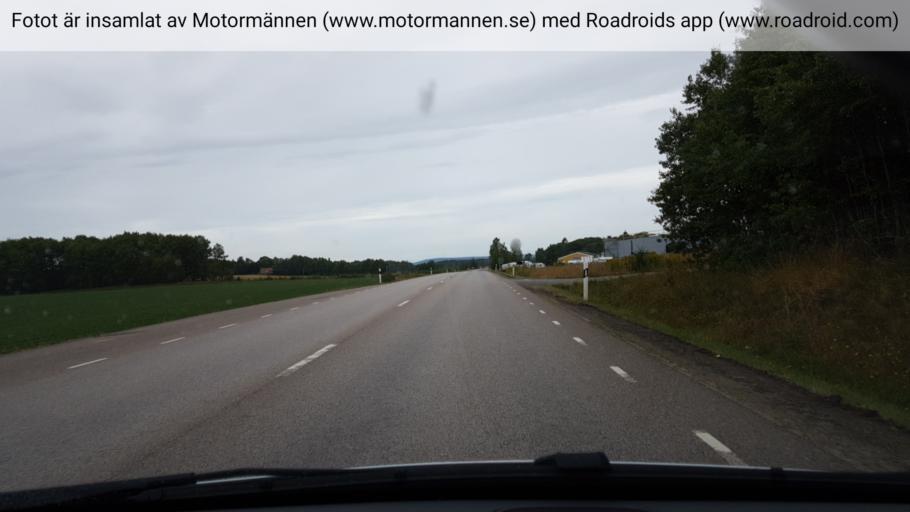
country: SE
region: Vaestra Goetaland
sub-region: Skovde Kommun
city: Stopen
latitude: 58.4052
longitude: 13.9960
